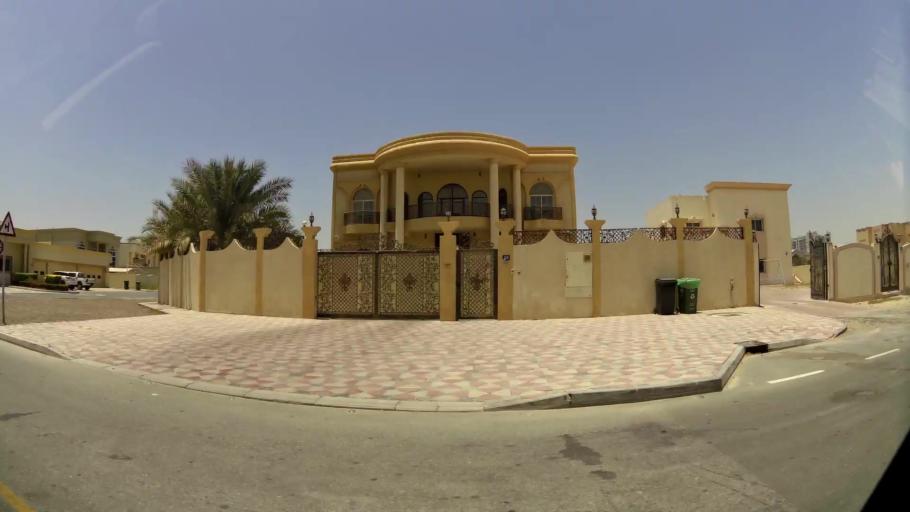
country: AE
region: Dubai
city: Dubai
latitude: 25.1006
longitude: 55.1960
